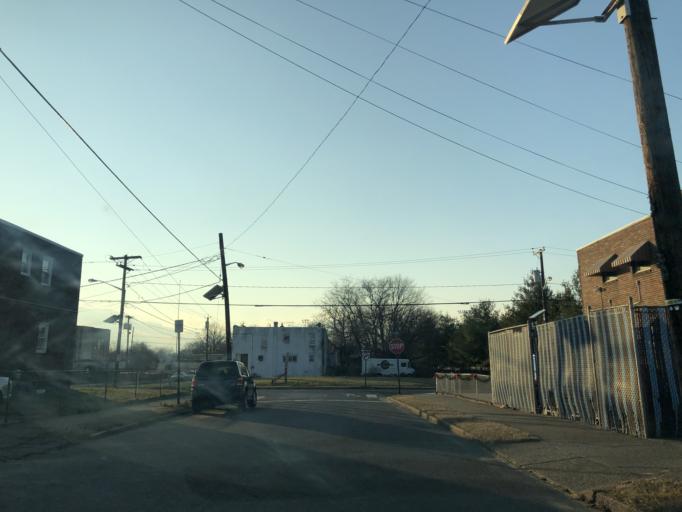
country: US
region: New Jersey
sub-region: Camden County
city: Camden
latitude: 39.9251
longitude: -75.1104
